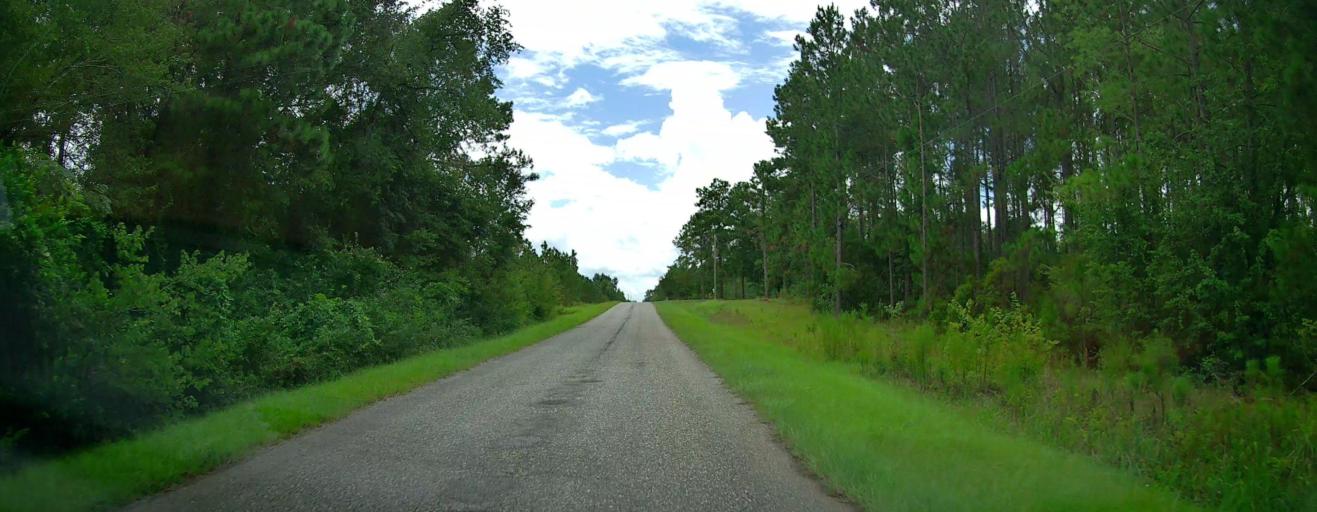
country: US
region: Georgia
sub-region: Dooly County
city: Vienna
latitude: 32.0650
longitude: -83.6276
